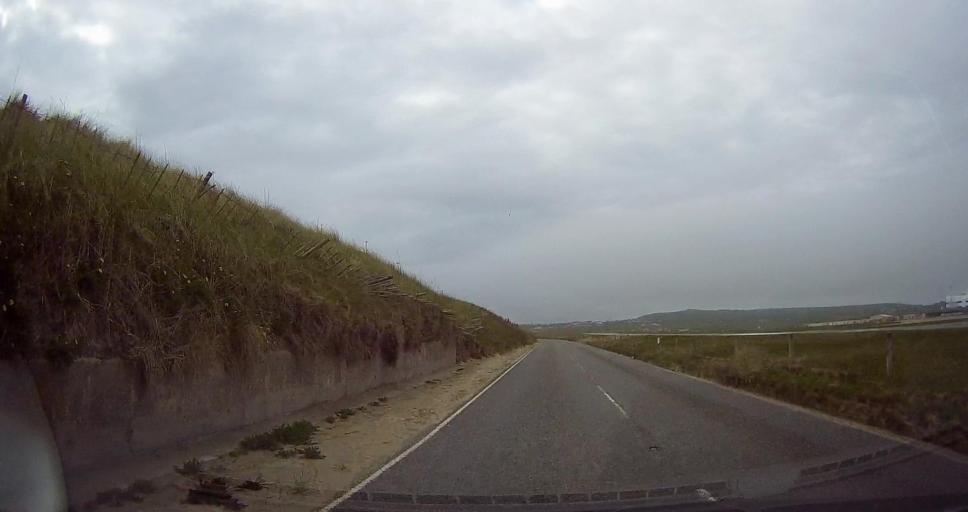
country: GB
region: Scotland
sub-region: Shetland Islands
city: Sandwick
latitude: 59.8735
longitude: -1.2900
